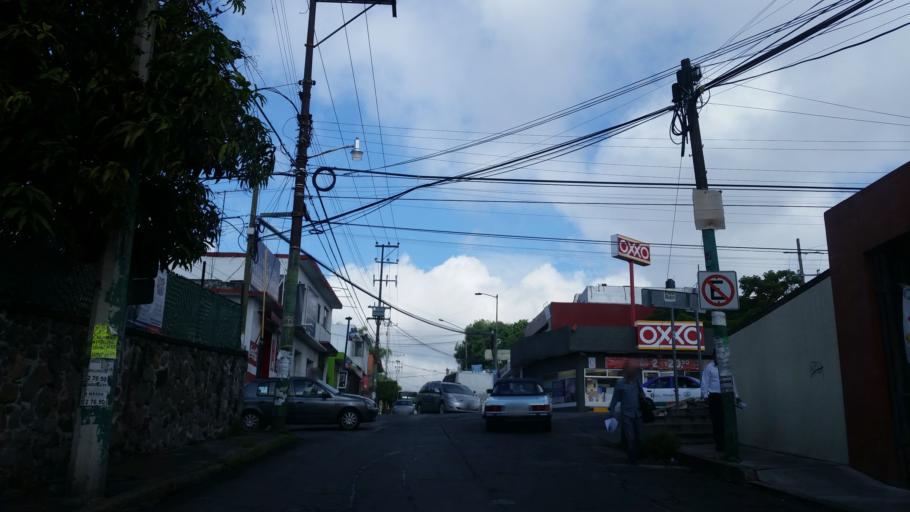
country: MX
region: Morelos
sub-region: Cuernavaca
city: Cuernavaca
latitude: 18.9204
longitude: -99.2115
